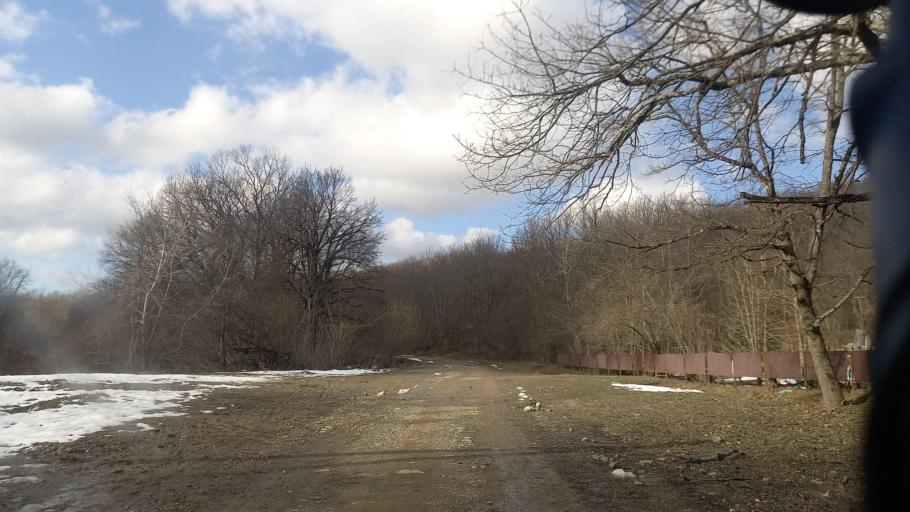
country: RU
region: Krasnodarskiy
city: Smolenskaya
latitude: 44.6008
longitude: 38.8751
